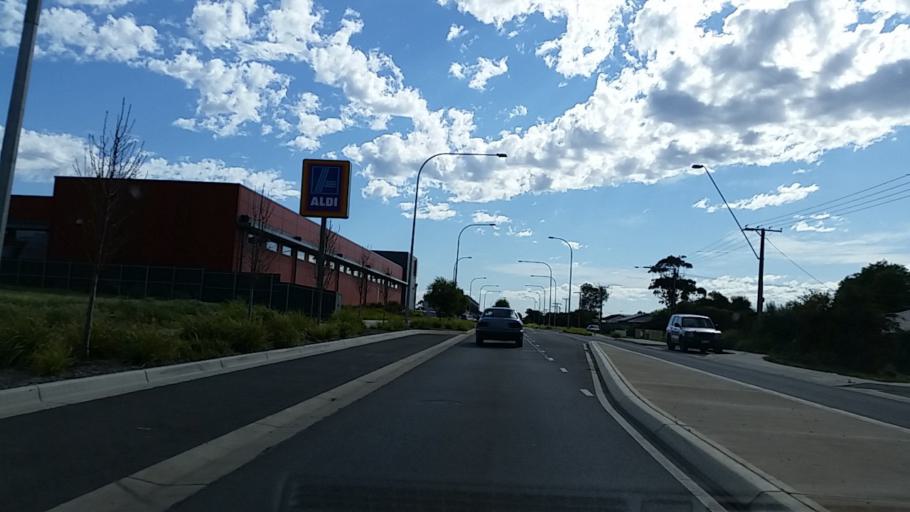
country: AU
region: South Australia
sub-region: Onkaparinga
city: Noarlunga
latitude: -35.1904
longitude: 138.4956
